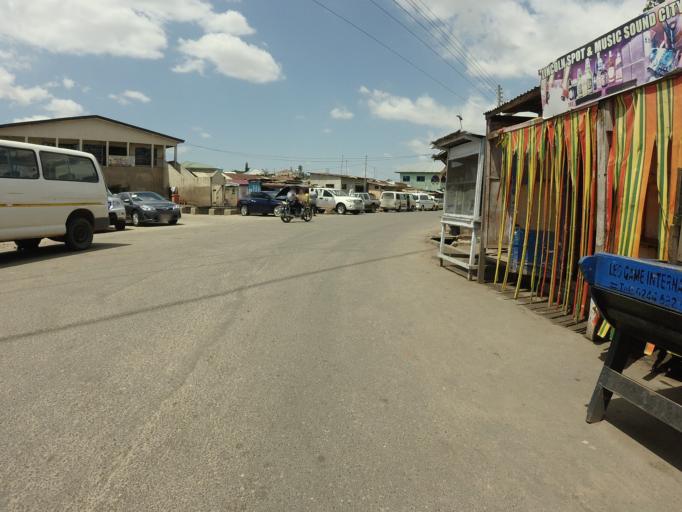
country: GH
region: Greater Accra
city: Accra
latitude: 5.5803
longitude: -0.2037
